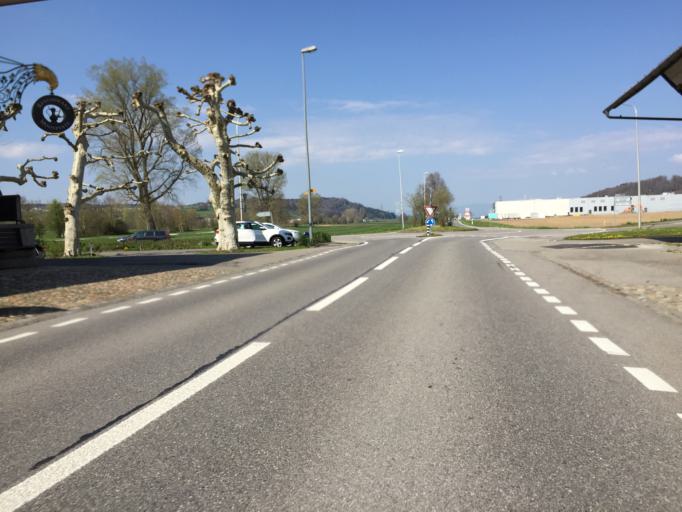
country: CH
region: Bern
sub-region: Bern-Mittelland District
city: Munchenbuchsee
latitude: 47.0295
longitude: 7.4603
